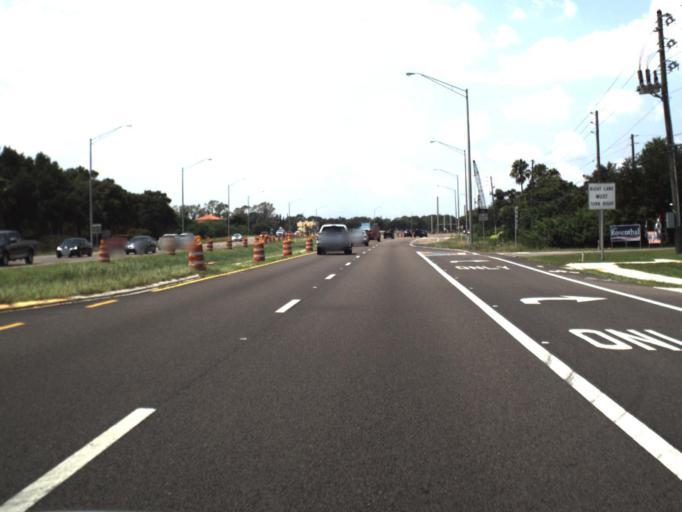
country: US
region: Florida
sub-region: Pinellas County
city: Gandy
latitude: 27.8658
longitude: -82.6319
